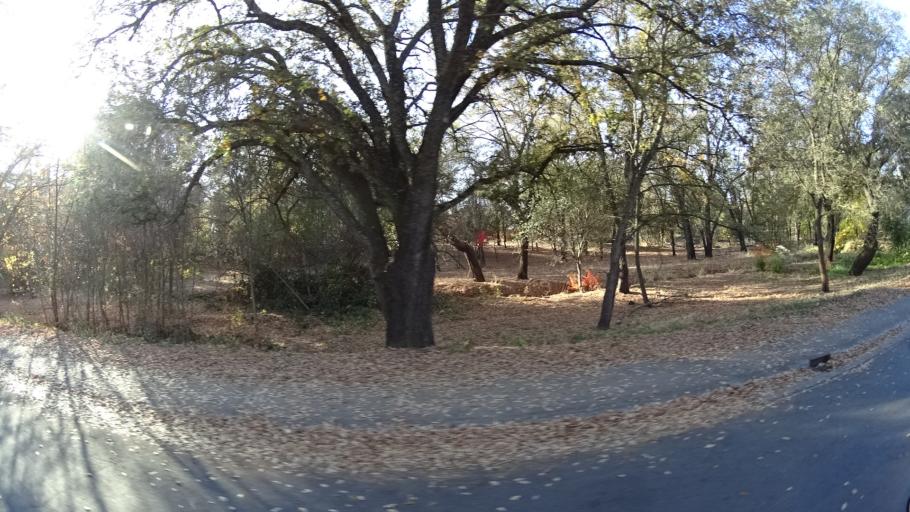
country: US
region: California
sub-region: Sacramento County
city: Citrus Heights
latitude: 38.7190
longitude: -121.2593
